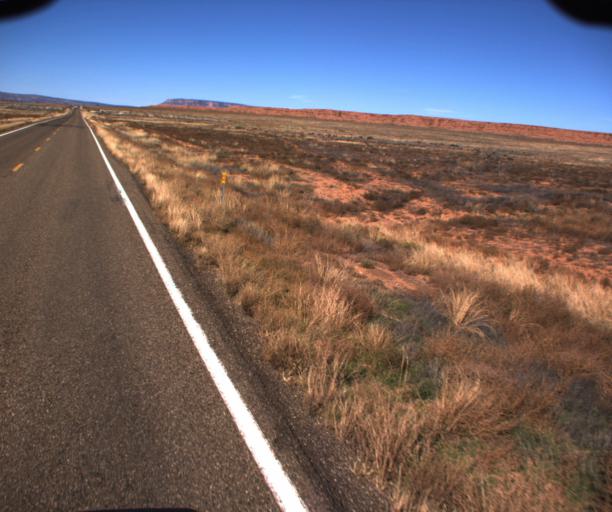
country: US
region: Arizona
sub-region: Coconino County
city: Fredonia
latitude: 36.9260
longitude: -112.4691
